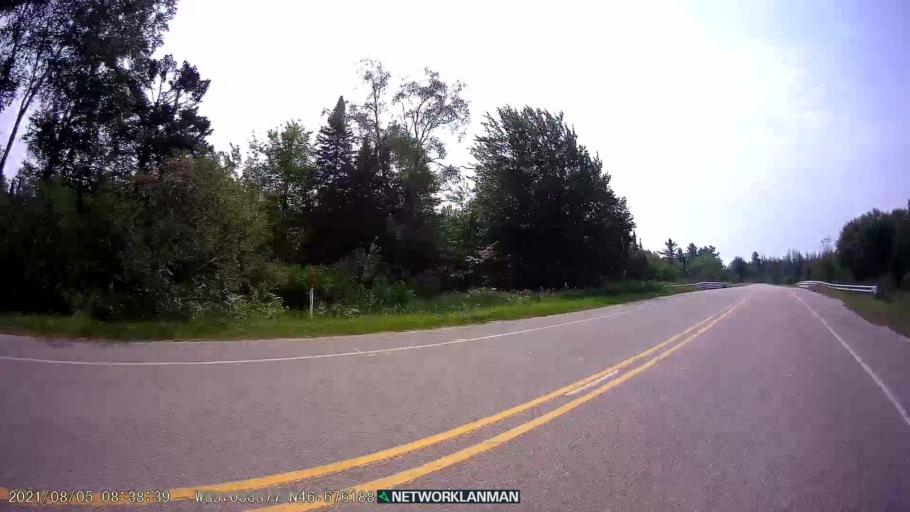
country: US
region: Michigan
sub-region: Luce County
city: Newberry
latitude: 46.6757
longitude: -85.0336
